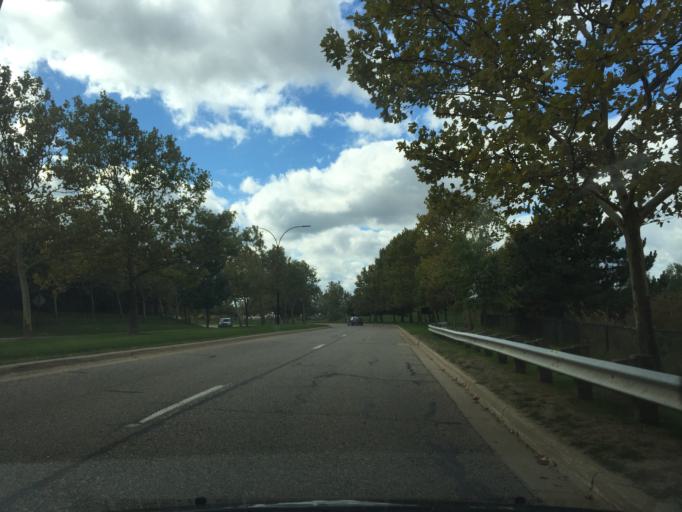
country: US
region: Michigan
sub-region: Oakland County
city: Auburn Hills
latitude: 42.6532
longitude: -83.2361
